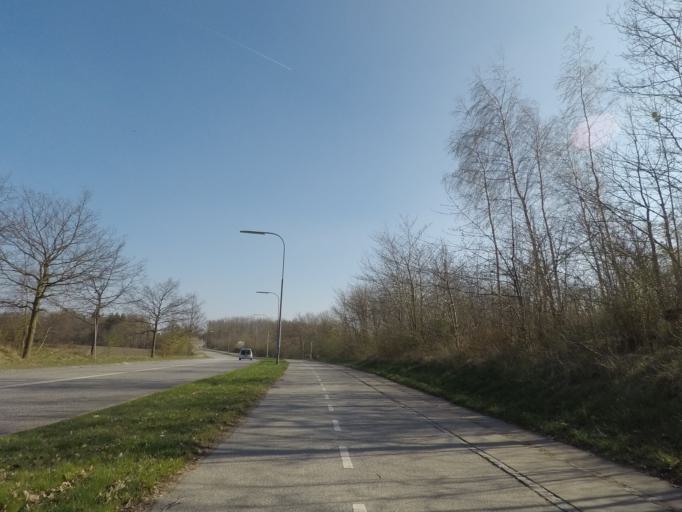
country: DK
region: Capital Region
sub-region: Ballerup Kommune
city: Ballerup
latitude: 55.7462
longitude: 12.3841
